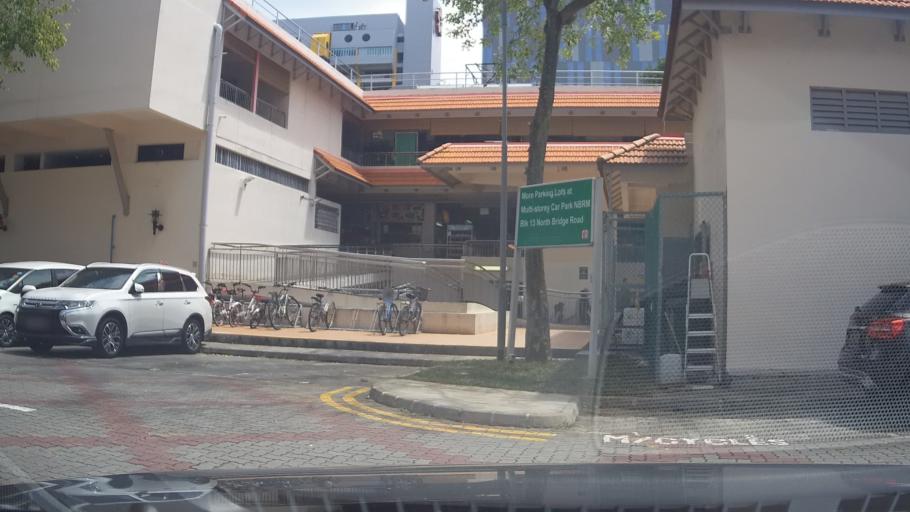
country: SG
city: Singapore
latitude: 1.3035
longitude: 103.8634
